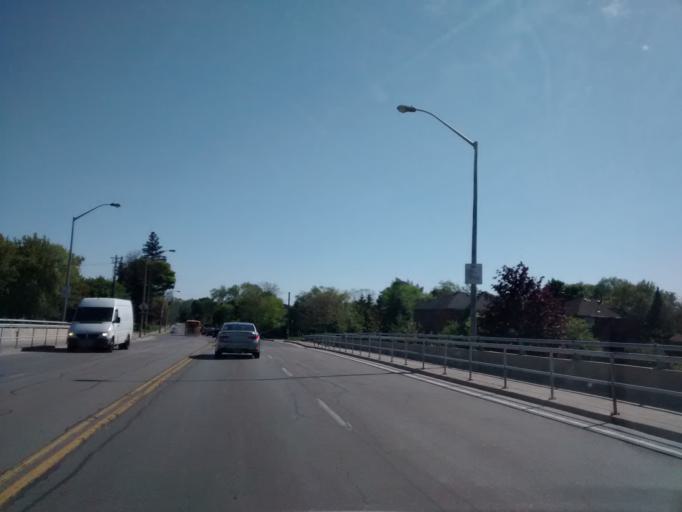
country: CA
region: Ontario
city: Oakville
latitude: 43.3921
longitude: -79.7141
